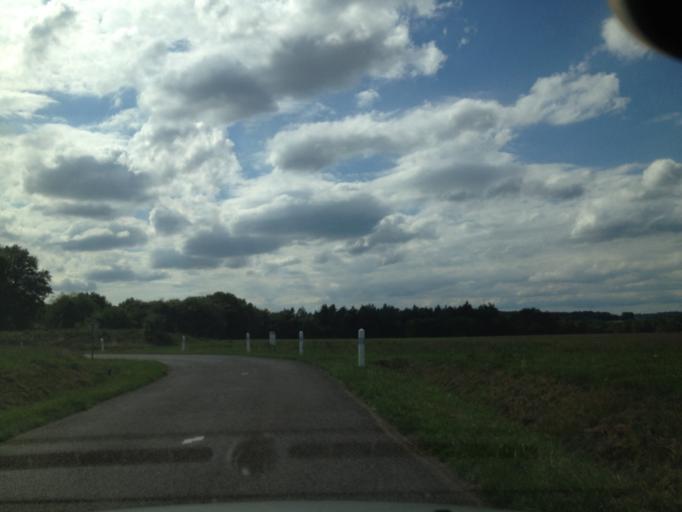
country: FR
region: Franche-Comte
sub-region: Departement de la Haute-Saone
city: Saint-Loup-sur-Semouse
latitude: 47.9047
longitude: 6.1696
